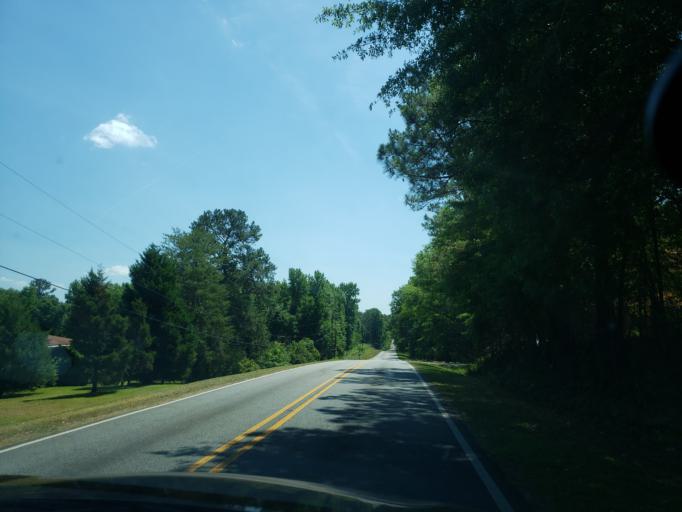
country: US
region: Alabama
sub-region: Elmore County
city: Tallassee
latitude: 32.5805
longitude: -85.8520
